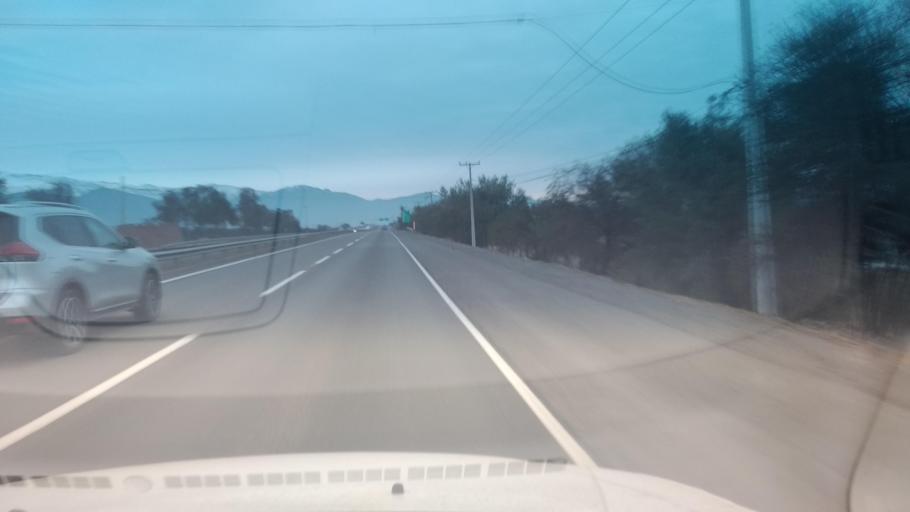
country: CL
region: Santiago Metropolitan
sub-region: Provincia de Chacabuco
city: Chicureo Abajo
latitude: -33.1396
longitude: -70.6635
